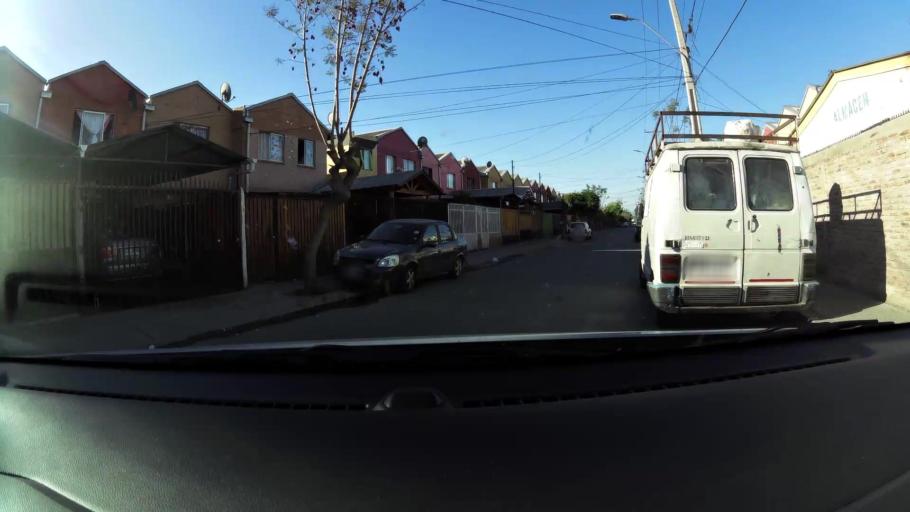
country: CL
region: Santiago Metropolitan
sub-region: Provincia de Maipo
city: San Bernardo
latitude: -33.6036
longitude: -70.6776
